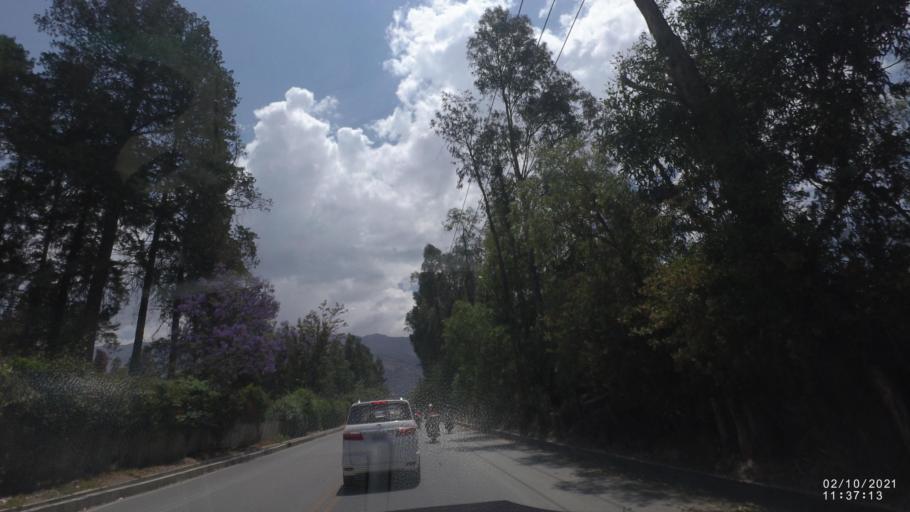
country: BO
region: Cochabamba
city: Cochabamba
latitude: -17.3445
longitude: -66.2233
